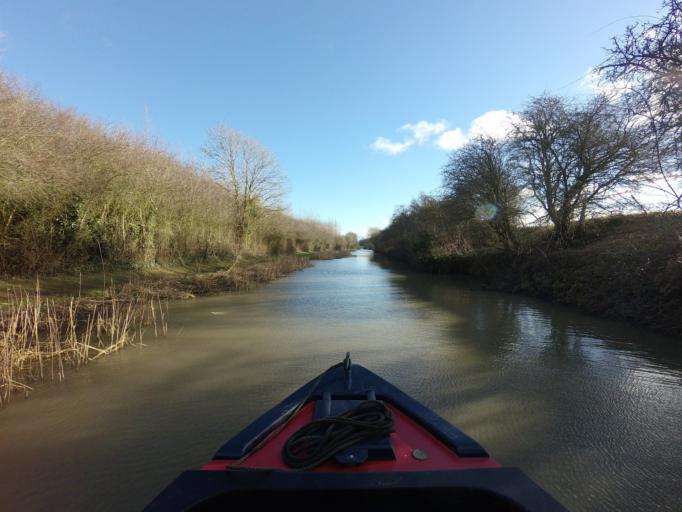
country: GB
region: England
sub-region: Northamptonshire
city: Blisworth
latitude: 52.1954
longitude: -0.9682
